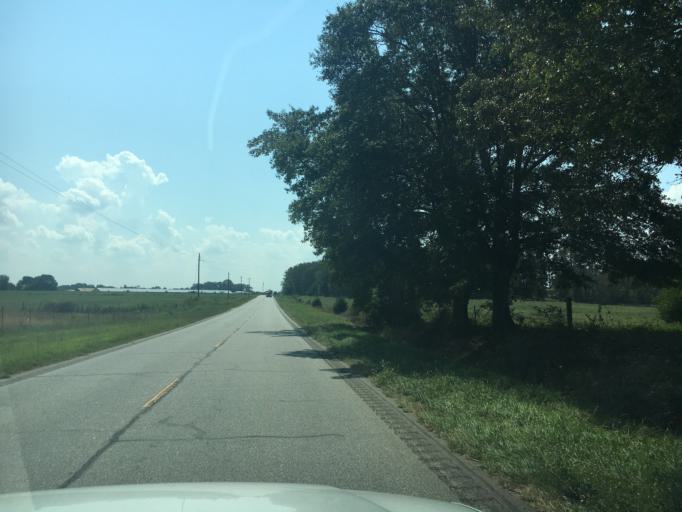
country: US
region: South Carolina
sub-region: Anderson County
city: Homeland Park
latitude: 34.4420
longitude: -82.7951
